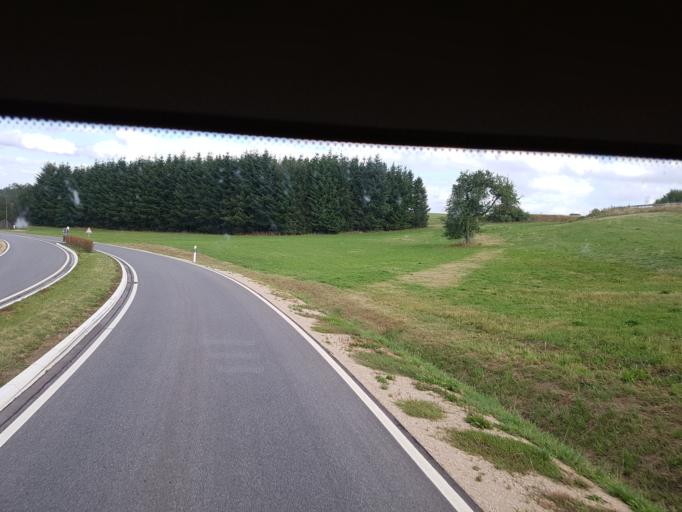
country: DE
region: Rheinland-Pfalz
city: Hinterweiler
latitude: 50.2466
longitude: 6.7607
